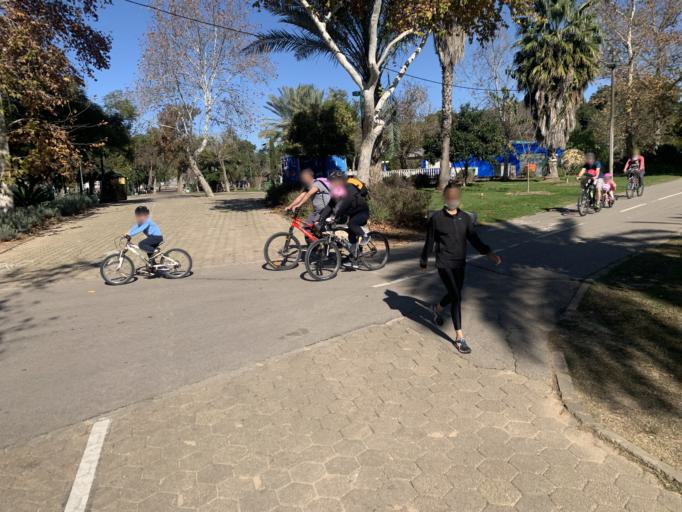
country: IL
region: Tel Aviv
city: Ramat Gan
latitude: 32.1002
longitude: 34.8089
